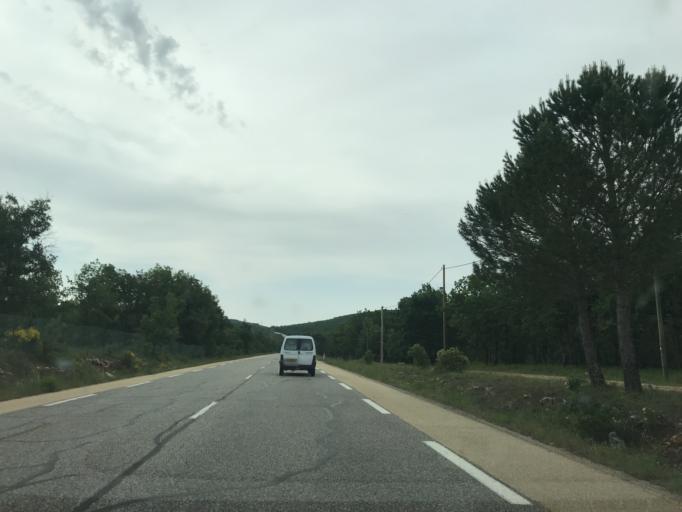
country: FR
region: Provence-Alpes-Cote d'Azur
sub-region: Departement du Var
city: Rians
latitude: 43.5538
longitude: 5.7943
